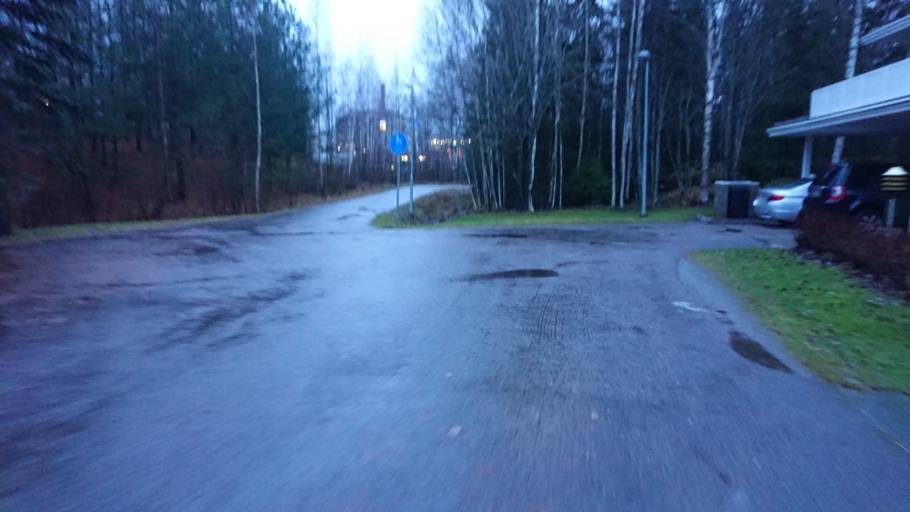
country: FI
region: Pirkanmaa
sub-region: Tampere
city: Tampere
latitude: 61.4446
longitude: 23.8598
